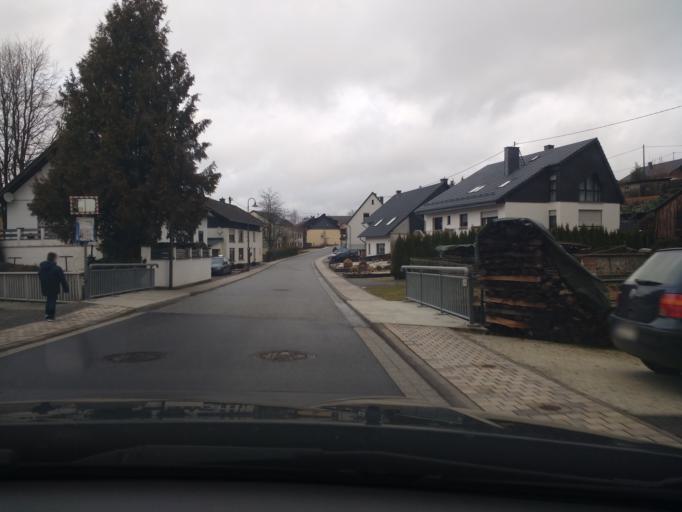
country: DE
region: Rheinland-Pfalz
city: Mandern
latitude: 49.6037
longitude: 6.7681
